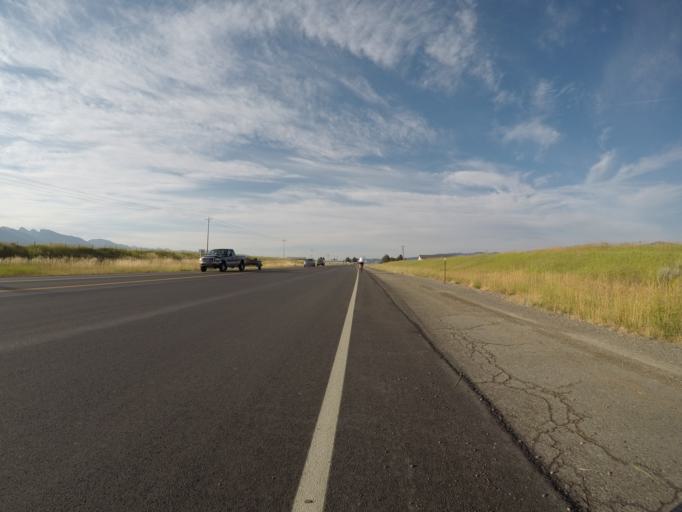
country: US
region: Wyoming
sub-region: Lincoln County
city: Afton
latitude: 42.9815
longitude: -111.0125
